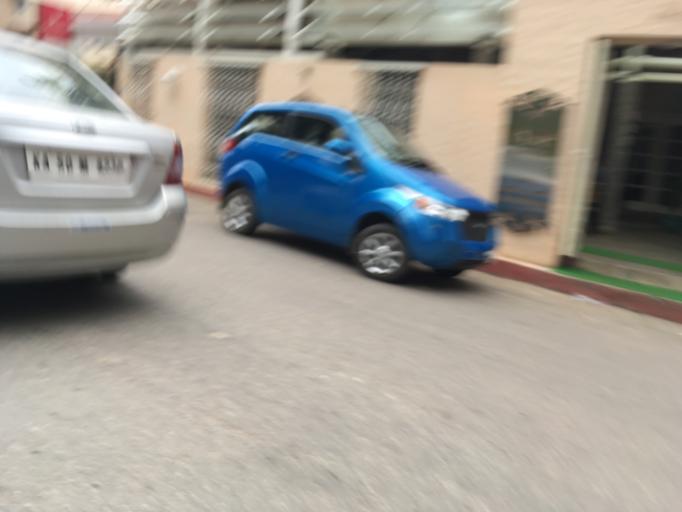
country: IN
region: Karnataka
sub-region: Bangalore Urban
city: Bangalore
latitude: 12.9699
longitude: 77.5975
